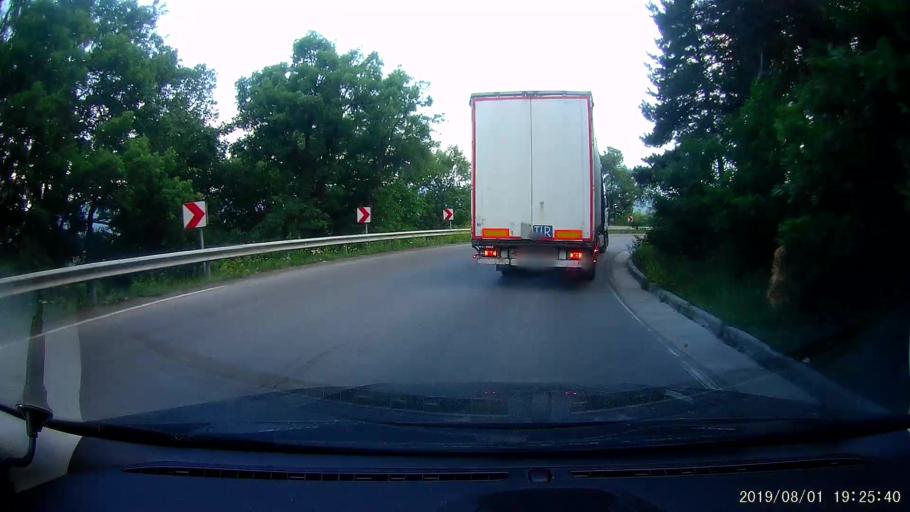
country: BG
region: Burgas
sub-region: Obshtina Sungurlare
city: Sungurlare
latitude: 42.8590
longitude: 26.9463
